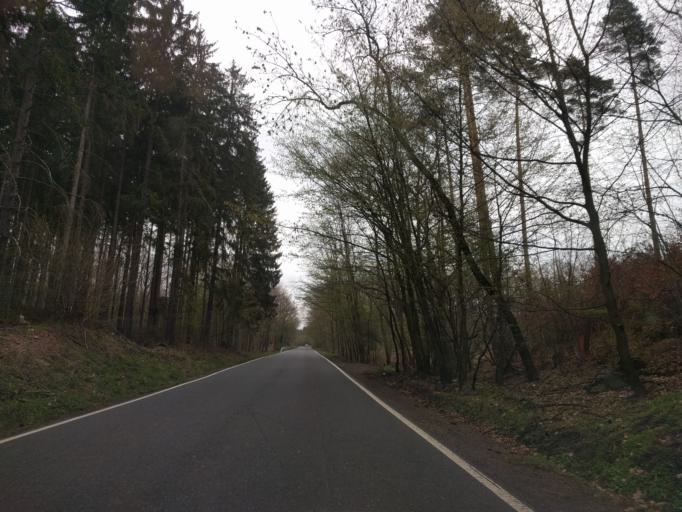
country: CZ
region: Central Bohemia
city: Vsenory
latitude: 49.9187
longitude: 14.3184
